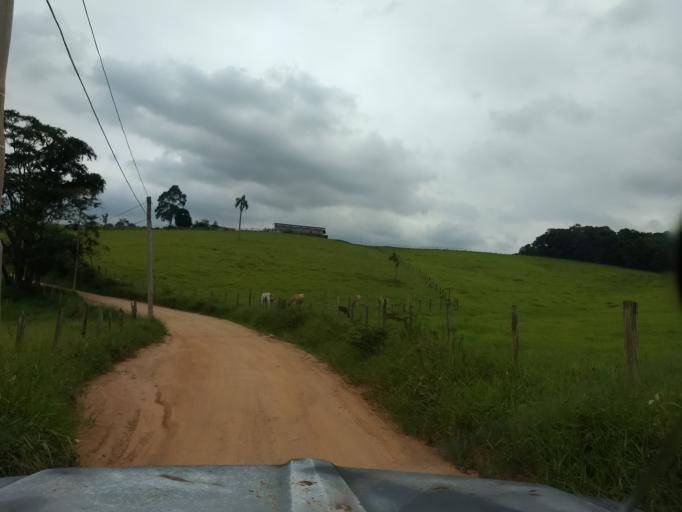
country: BR
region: Sao Paulo
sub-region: Cabreuva
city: Cabreuva
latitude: -23.3876
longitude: -47.1838
